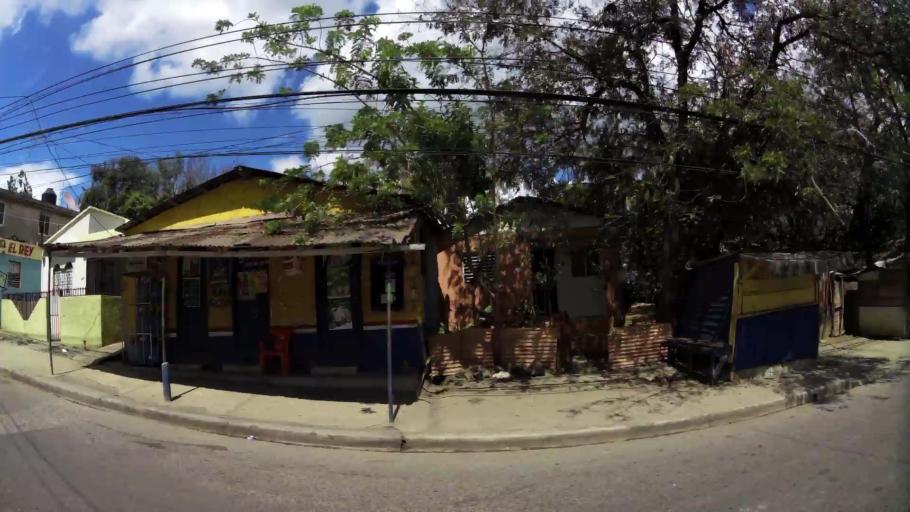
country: DO
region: Santiago
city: Santiago de los Caballeros
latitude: 19.4091
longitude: -70.6715
